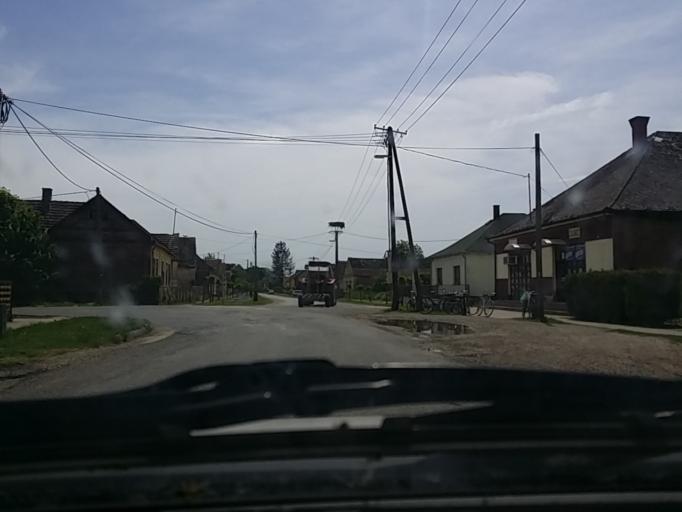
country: HU
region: Somogy
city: Barcs
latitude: 45.9534
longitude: 17.6168
